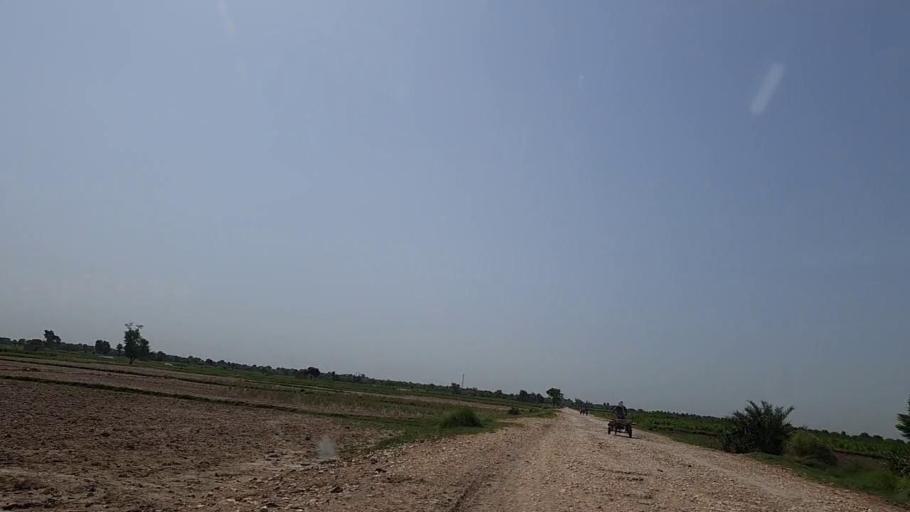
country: PK
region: Sindh
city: Naushahro Firoz
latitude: 26.8413
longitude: 68.0152
